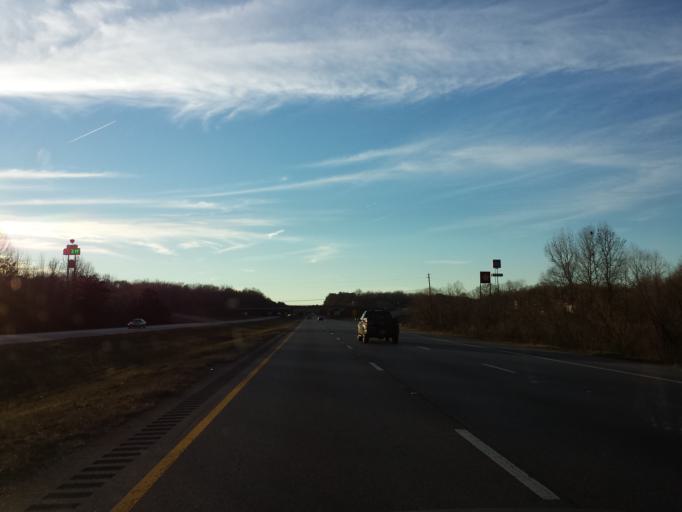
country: US
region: Mississippi
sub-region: Lauderdale County
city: Marion
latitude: 32.4137
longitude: -88.5020
